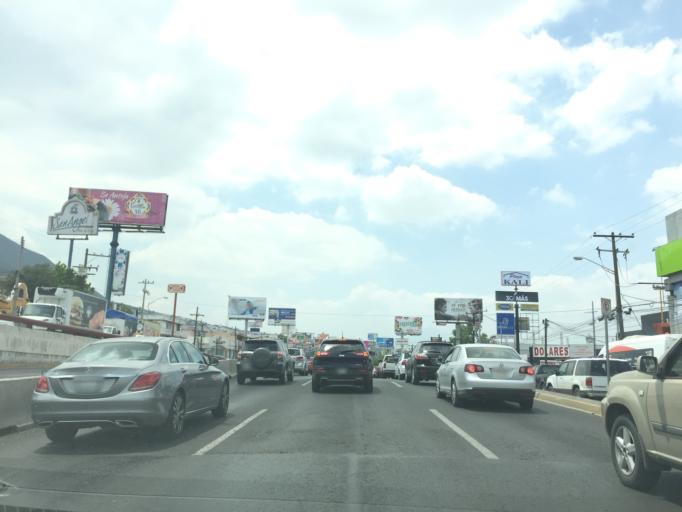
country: MX
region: Nuevo Leon
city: Garza Garcia
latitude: 25.7058
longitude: -100.3705
